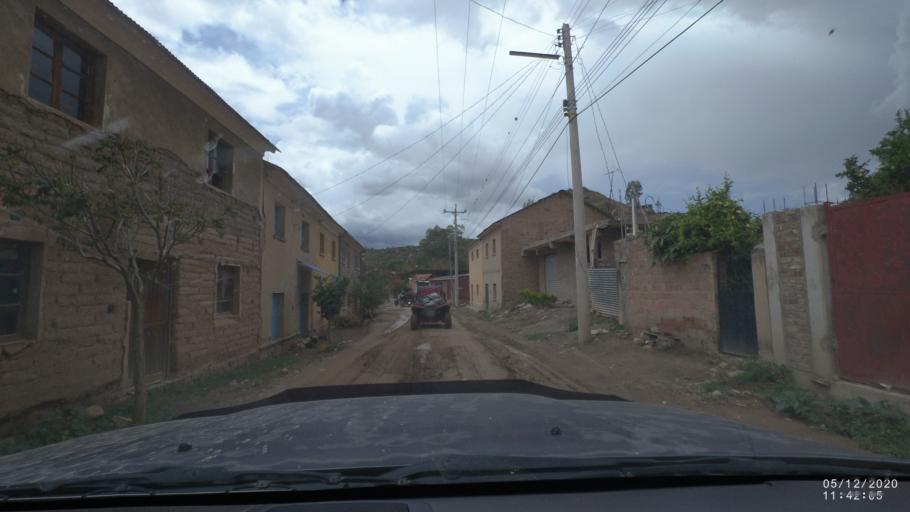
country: BO
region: Cochabamba
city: Sipe Sipe
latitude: -17.5529
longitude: -66.3414
